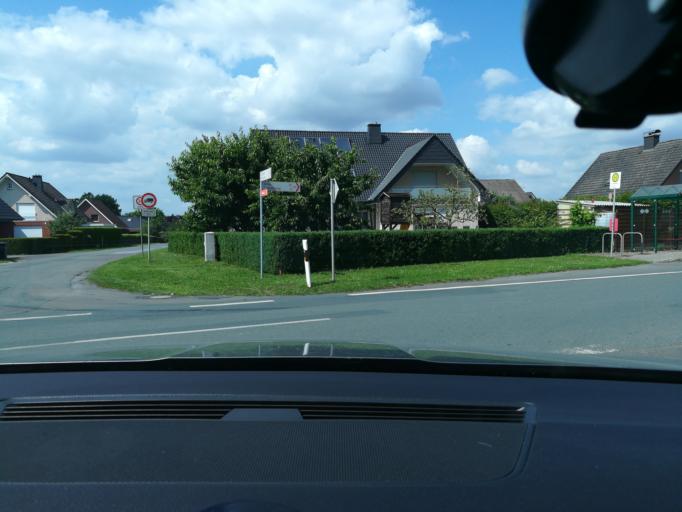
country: DE
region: North Rhine-Westphalia
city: Espelkamp
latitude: 52.3440
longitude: 8.6377
